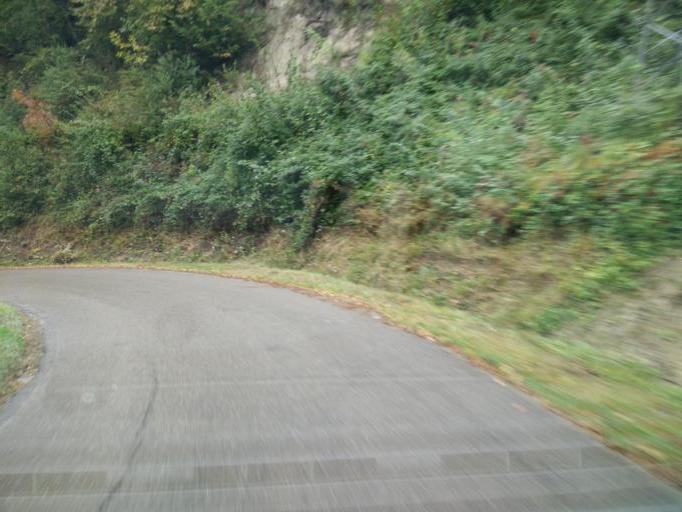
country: IT
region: Emilia-Romagna
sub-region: Provincia di Bologna
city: Marzabotto
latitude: 44.3123
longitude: 11.1918
